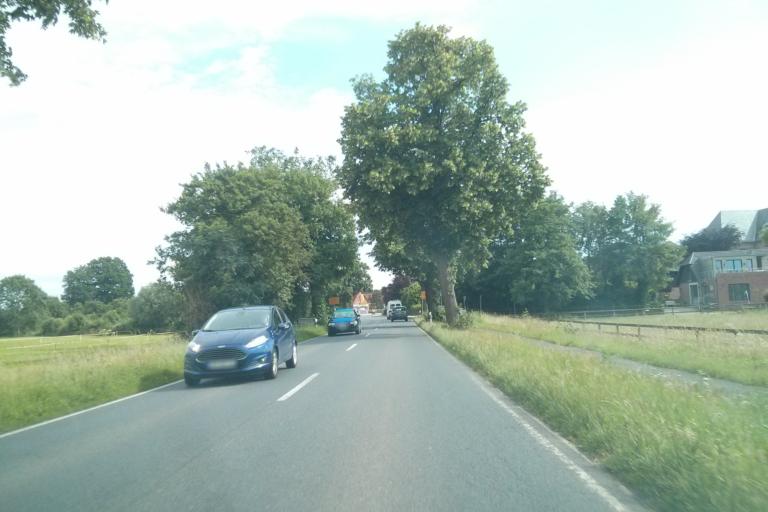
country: DE
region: Lower Saxony
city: Thedinghausen
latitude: 52.9697
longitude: 9.0485
